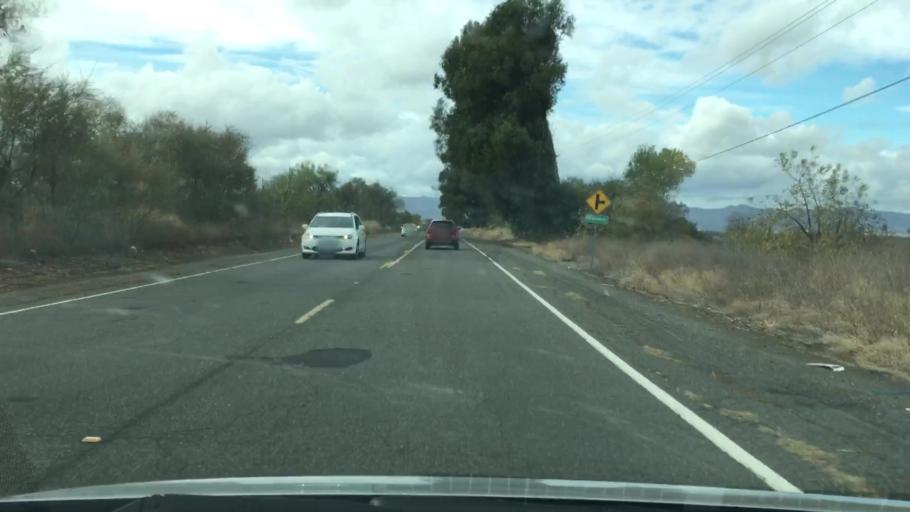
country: US
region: California
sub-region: Yolo County
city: Winters
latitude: 38.5616
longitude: -121.8840
